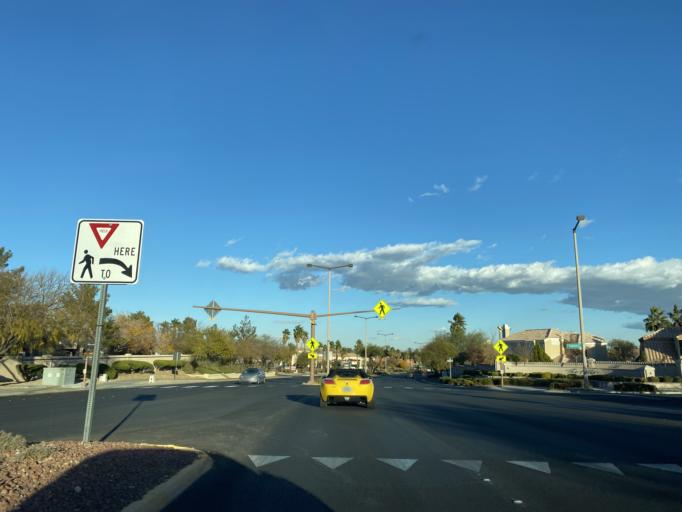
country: US
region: Nevada
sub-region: Clark County
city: Summerlin South
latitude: 36.2057
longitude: -115.3050
